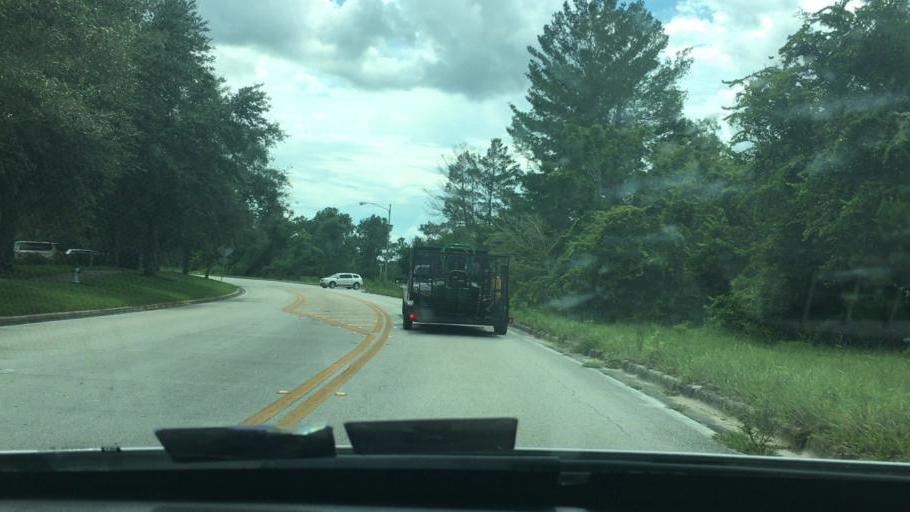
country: US
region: Florida
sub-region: Orange County
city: Alafaya
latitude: 28.6082
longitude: -81.2124
